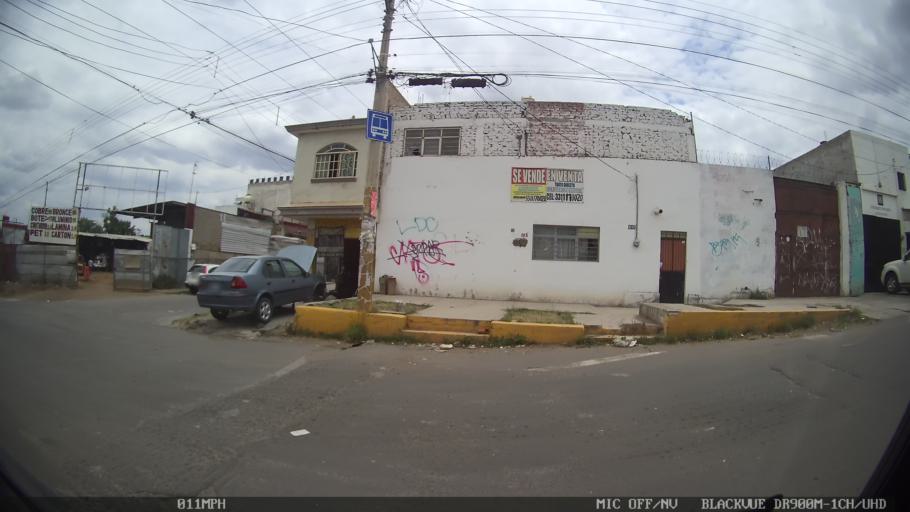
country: MX
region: Jalisco
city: Tlaquepaque
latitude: 20.6452
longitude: -103.2644
